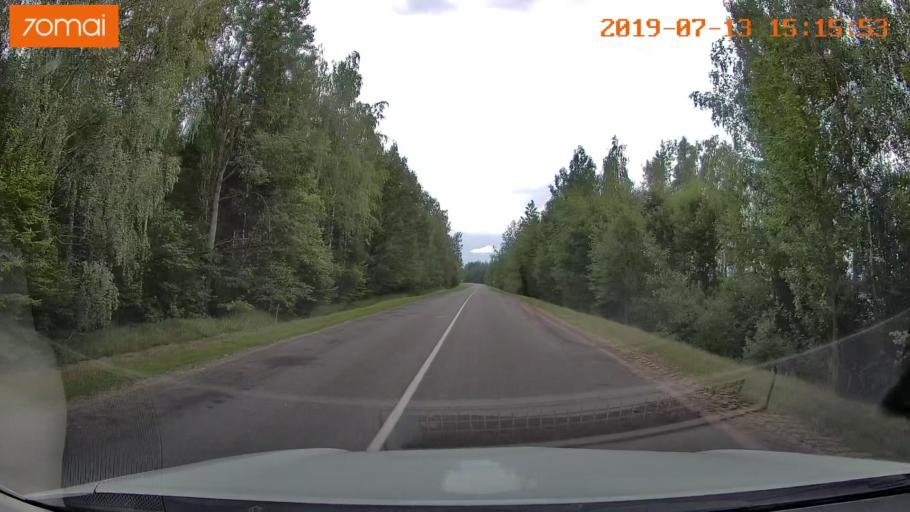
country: BY
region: Mogilev
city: Hlusha
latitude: 53.1137
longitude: 28.8290
